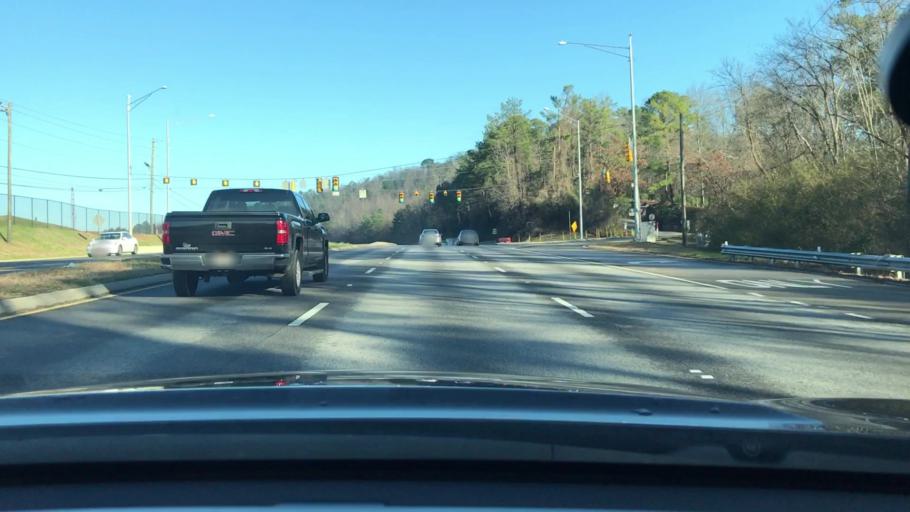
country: US
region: Alabama
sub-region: Jefferson County
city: Cahaba Heights
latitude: 33.4638
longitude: -86.7571
